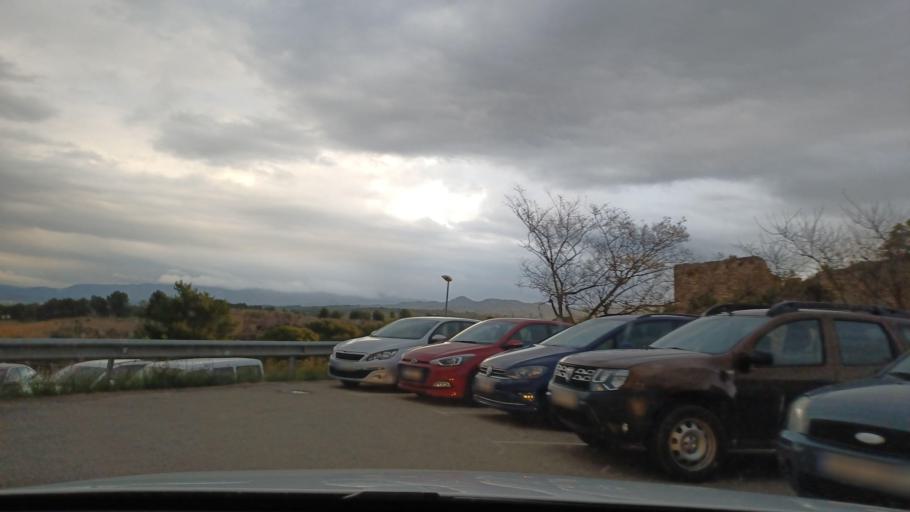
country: ES
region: Catalonia
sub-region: Provincia de Tarragona
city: Tortosa
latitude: 40.8123
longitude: 0.5260
